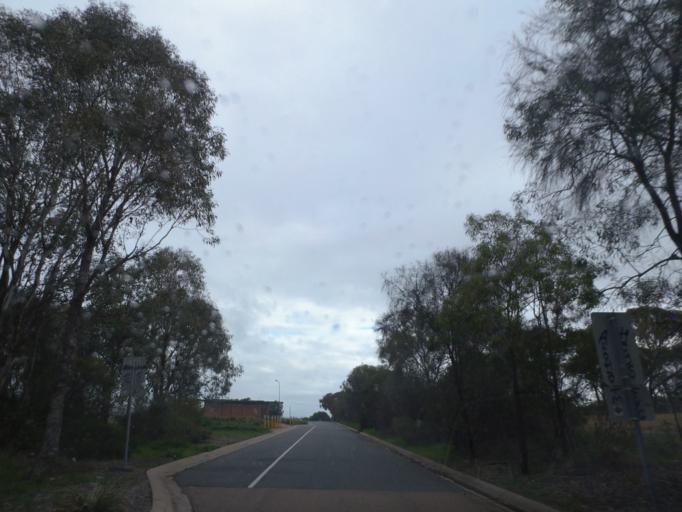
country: AU
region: Victoria
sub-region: Wangaratta
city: Wangaratta
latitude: -36.2211
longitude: 146.4463
